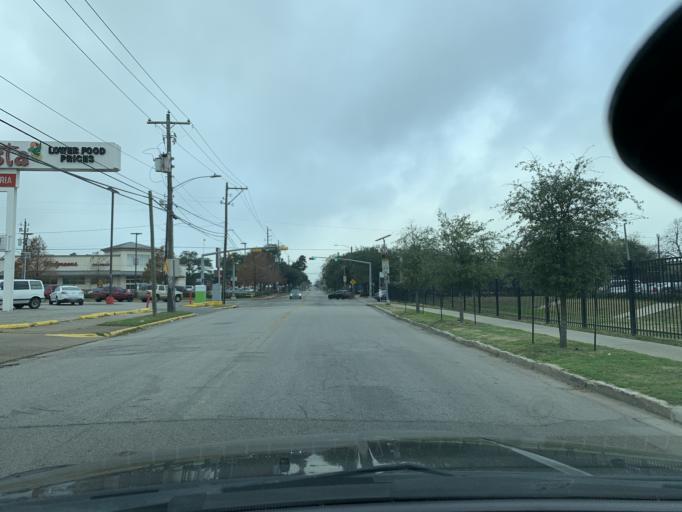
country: US
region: Texas
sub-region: Harris County
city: Houston
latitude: 29.7833
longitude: -95.3545
